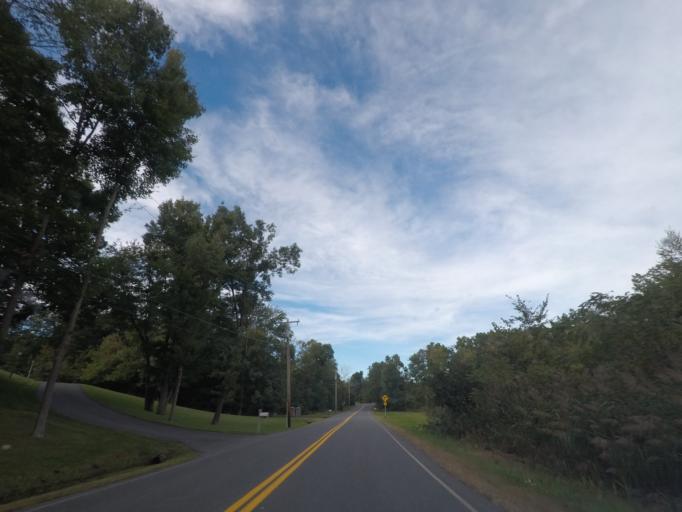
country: US
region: New York
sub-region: Rensselaer County
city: East Greenbush
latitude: 42.6027
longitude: -73.6770
